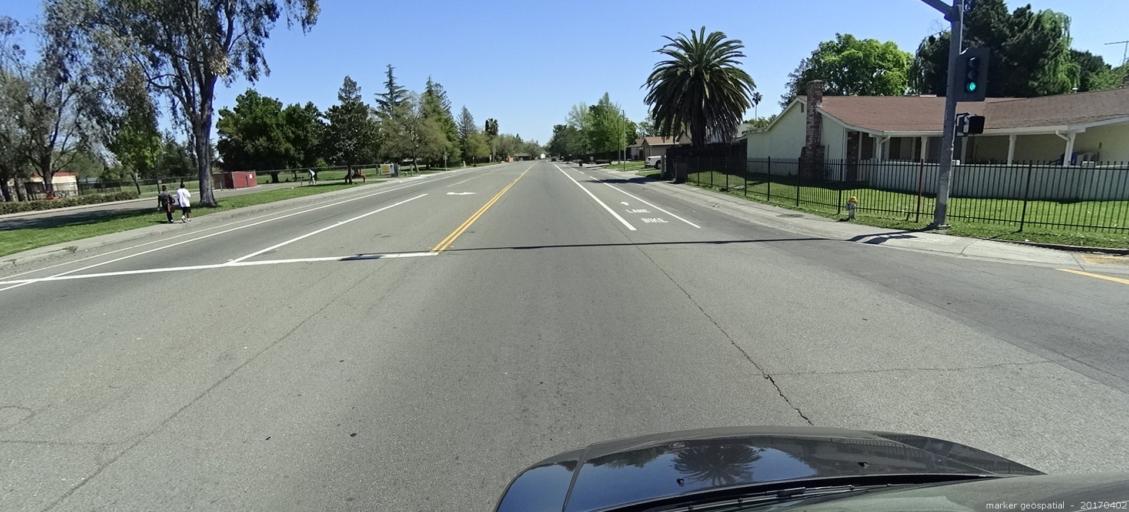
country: US
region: California
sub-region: Sacramento County
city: Parkway
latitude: 38.4659
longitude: -121.4398
